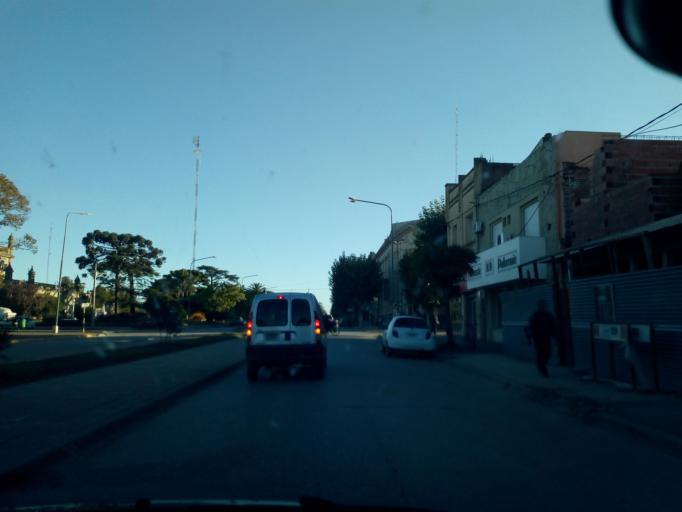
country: AR
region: Buenos Aires
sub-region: Partido de Loberia
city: Loberia
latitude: -38.1632
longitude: -58.7826
